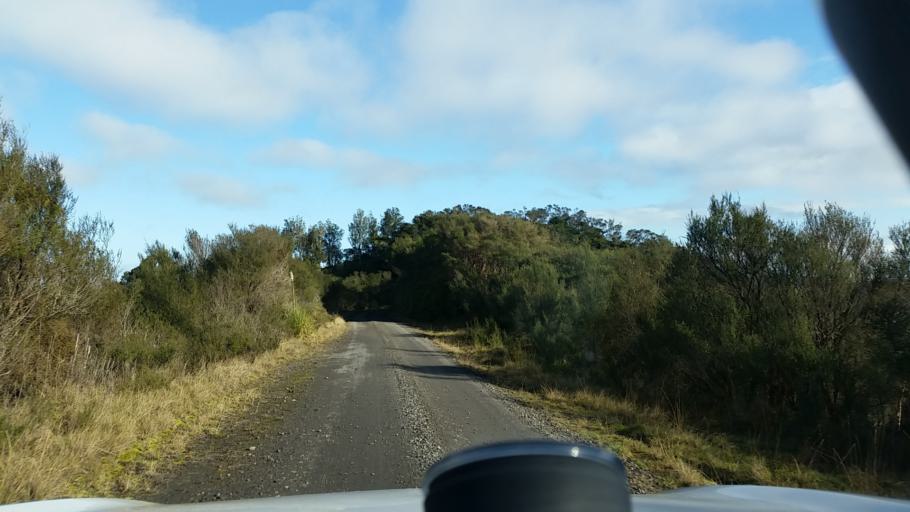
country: NZ
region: Taranaki
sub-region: South Taranaki District
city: Eltham
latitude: -39.4073
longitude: 174.5547
